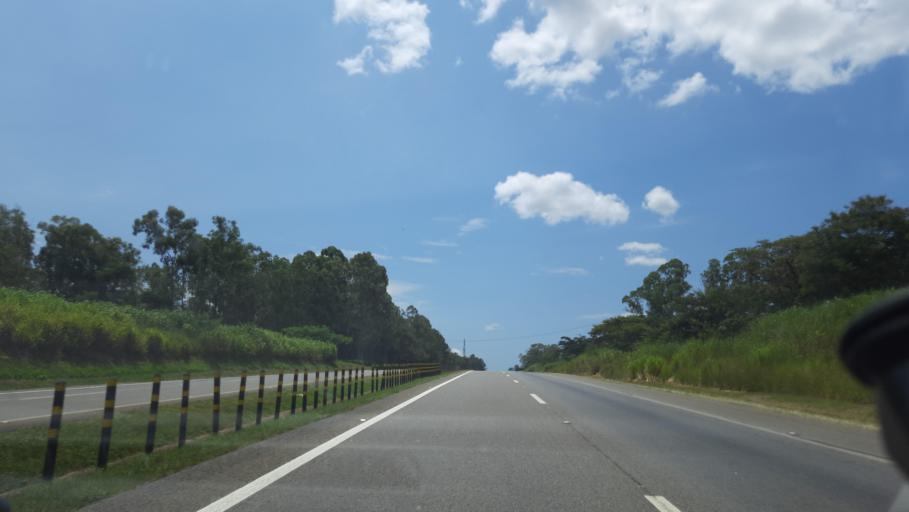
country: BR
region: Sao Paulo
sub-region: Mococa
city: Mococa
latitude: -21.5313
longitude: -47.0294
